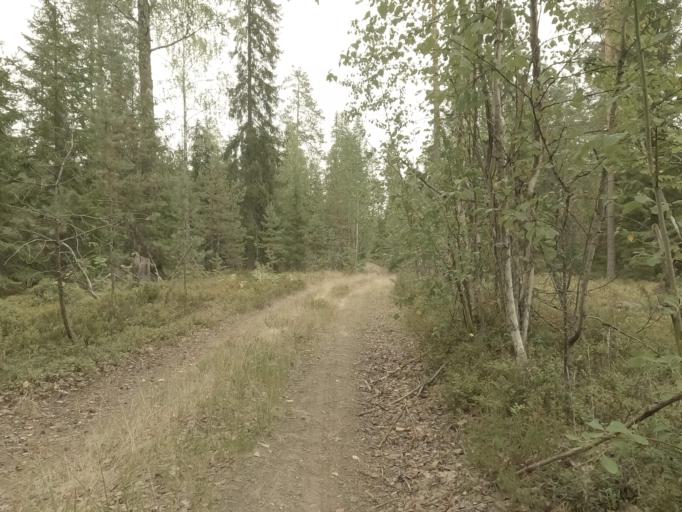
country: RU
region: Leningrad
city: Kamennogorsk
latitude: 61.0535
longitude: 29.1744
